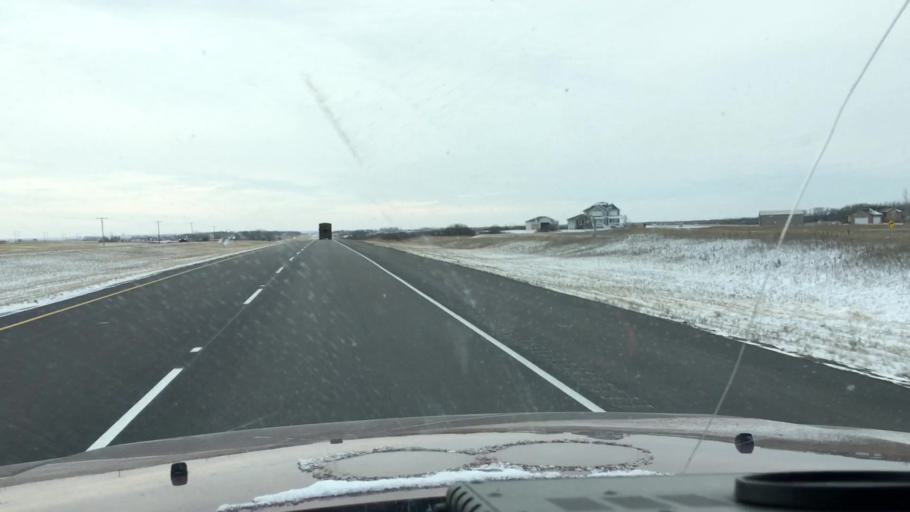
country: CA
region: Saskatchewan
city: Saskatoon
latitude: 51.9300
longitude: -106.5353
